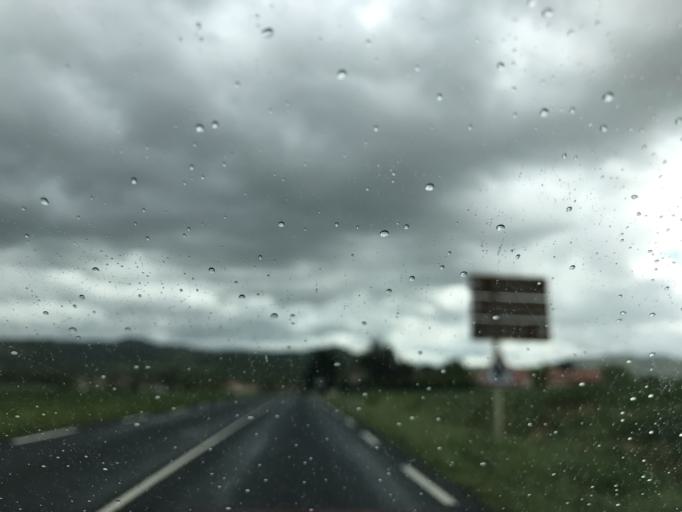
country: FR
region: Auvergne
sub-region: Departement du Puy-de-Dome
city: Billom
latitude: 45.7276
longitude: 3.3501
